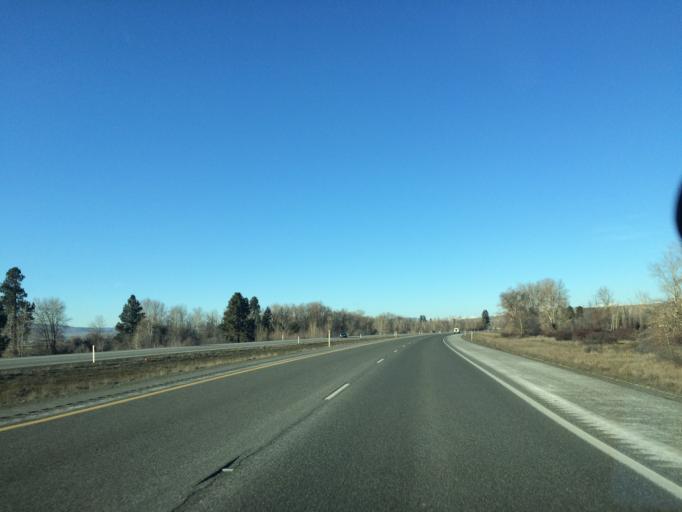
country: US
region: Washington
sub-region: Kittitas County
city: Ellensburg
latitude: 47.0317
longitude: -120.6225
